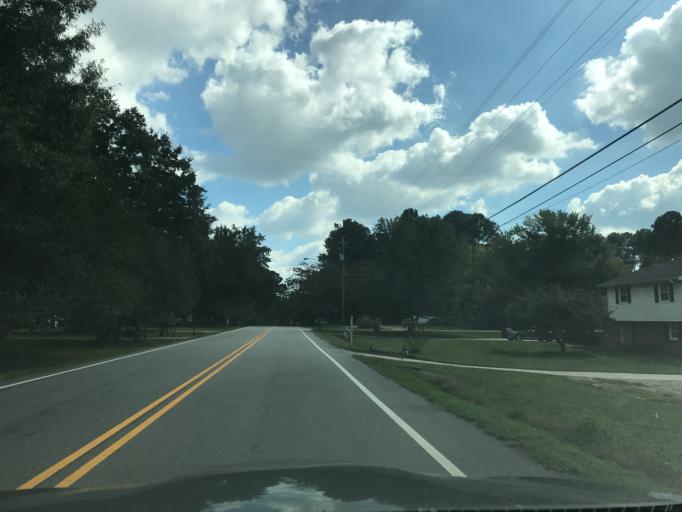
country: US
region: North Carolina
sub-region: Wake County
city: Wake Forest
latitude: 35.9482
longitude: -78.5303
